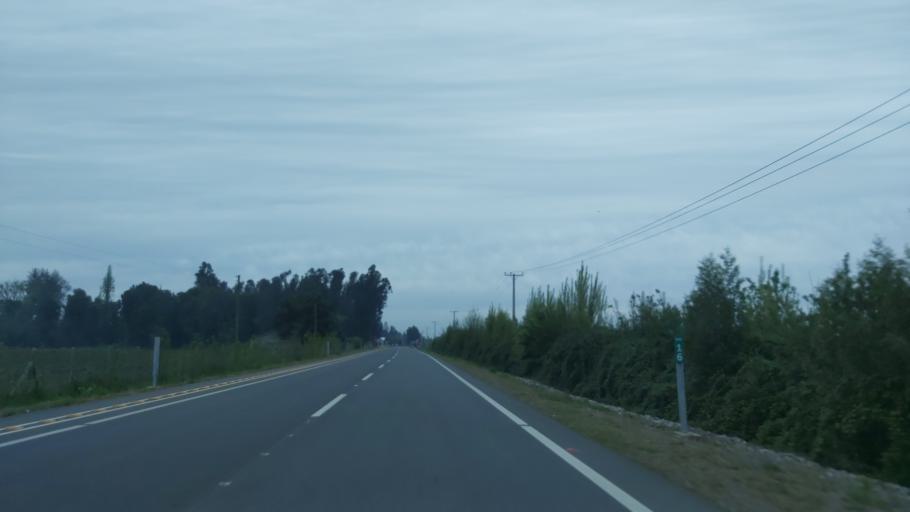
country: CL
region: Maule
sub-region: Provincia de Linares
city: Colbun
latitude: -35.7100
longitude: -71.4812
